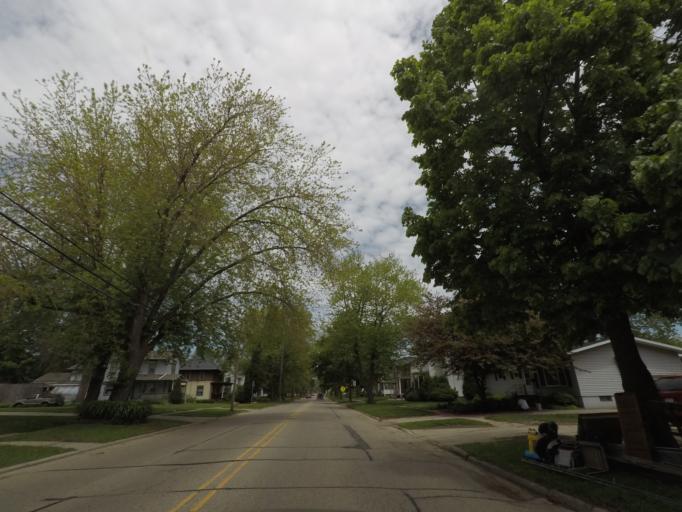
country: US
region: Wisconsin
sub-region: Rock County
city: Evansville
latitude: 42.7743
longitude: -89.2991
